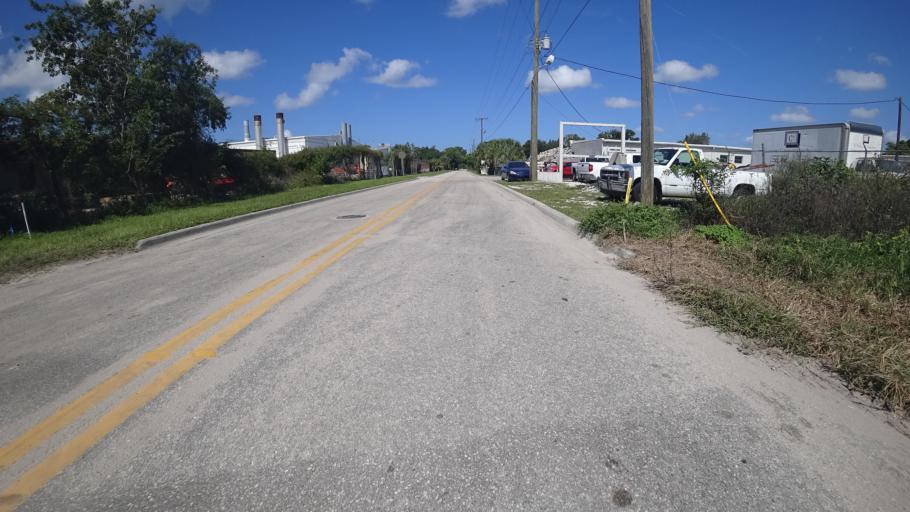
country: US
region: Florida
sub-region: Manatee County
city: Whitfield
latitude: 27.4220
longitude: -82.5426
